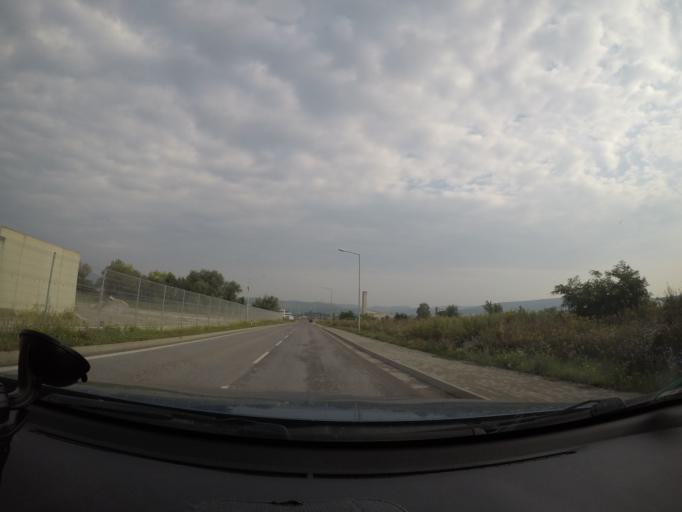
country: SK
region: Trenciansky
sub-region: Okres Trencin
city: Trencin
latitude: 48.8867
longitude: 18.0075
